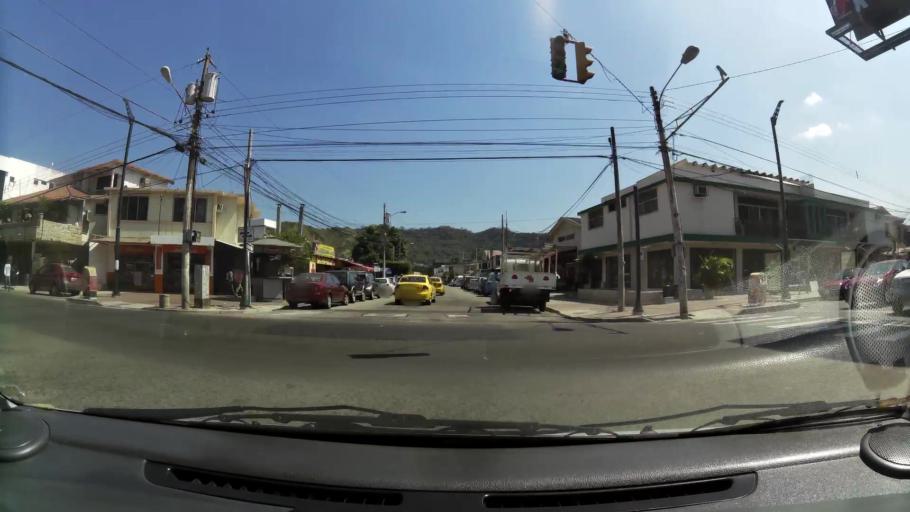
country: EC
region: Guayas
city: Guayaquil
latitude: -2.1658
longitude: -79.9115
